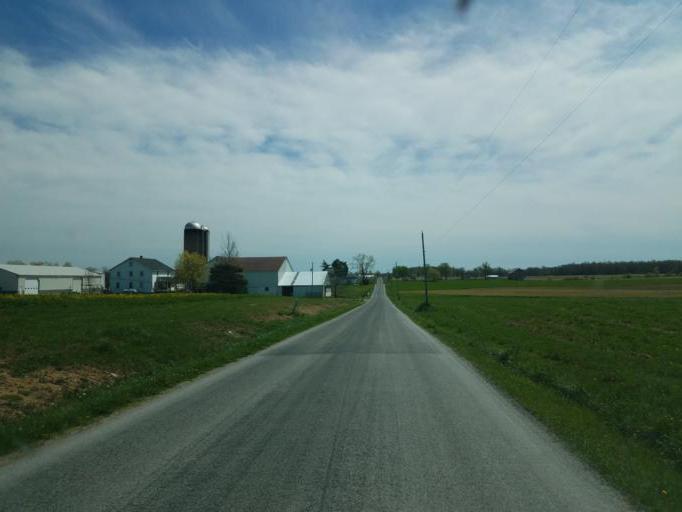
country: US
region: Ohio
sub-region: Huron County
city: Greenwich
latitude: 40.9129
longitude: -82.4552
